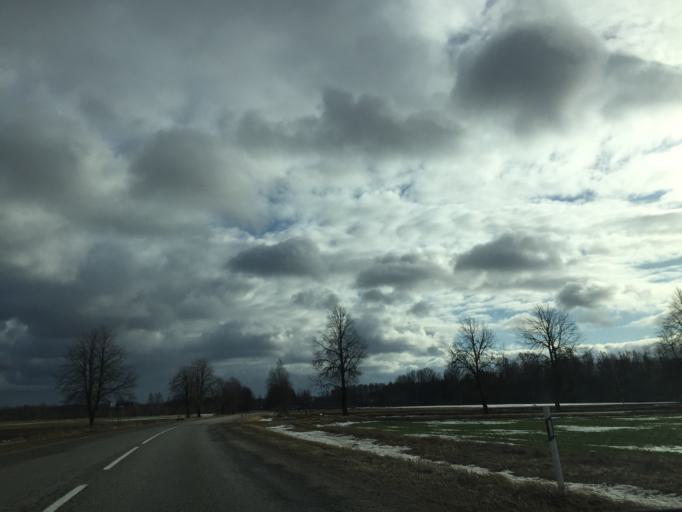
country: LV
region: Aloja
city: Staicele
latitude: 57.8874
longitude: 24.6536
